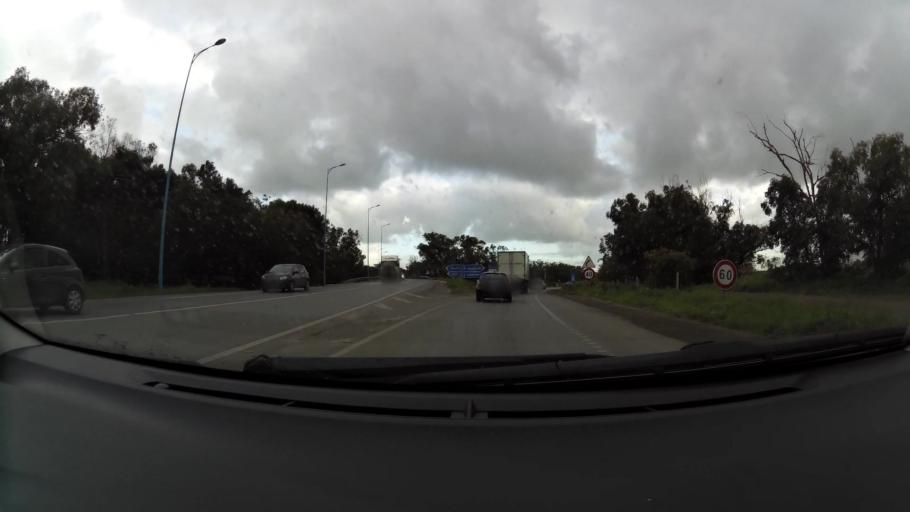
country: MA
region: Grand Casablanca
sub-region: Mohammedia
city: Mohammedia
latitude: 33.6636
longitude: -7.4045
